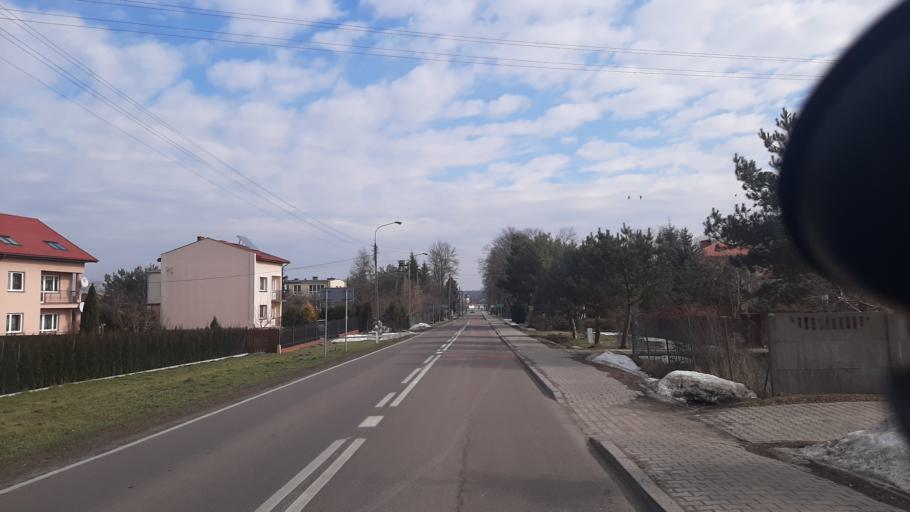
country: PL
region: Lublin Voivodeship
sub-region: Powiat lubelski
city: Niemce
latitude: 51.3586
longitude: 22.6154
